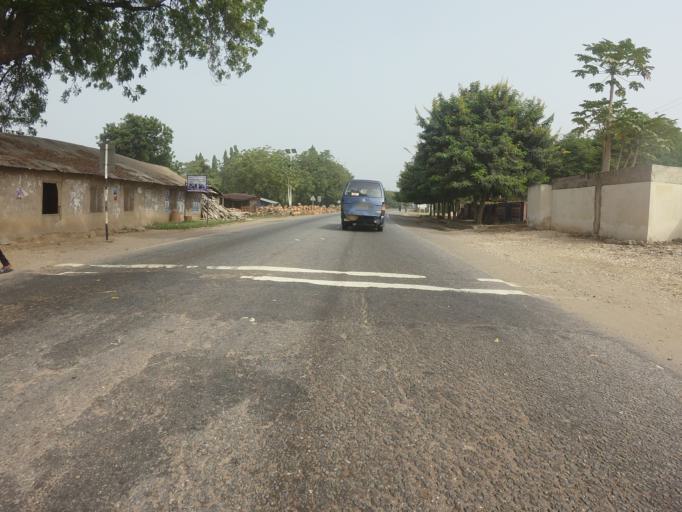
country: GH
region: Volta
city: Anloga
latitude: 6.0079
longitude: 0.5527
